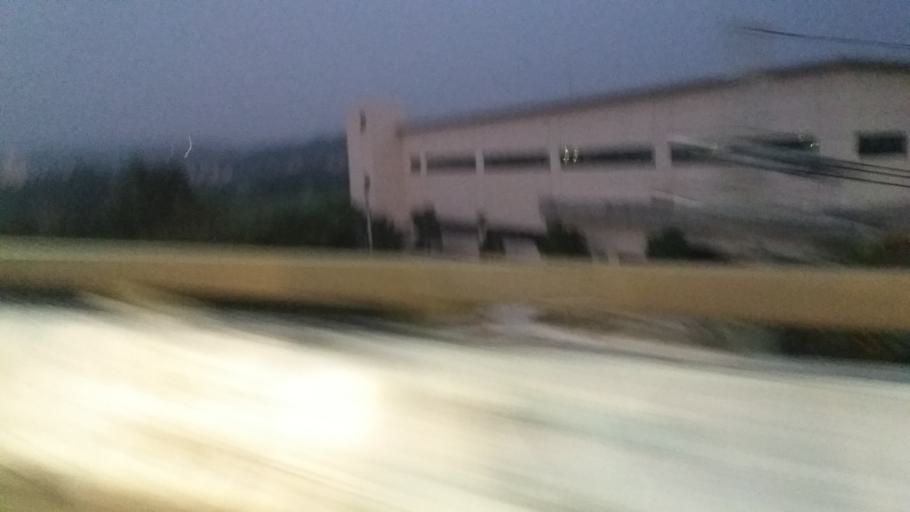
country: TW
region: Taiwan
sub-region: Hsinchu
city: Hsinchu
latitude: 24.7555
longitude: 120.9108
